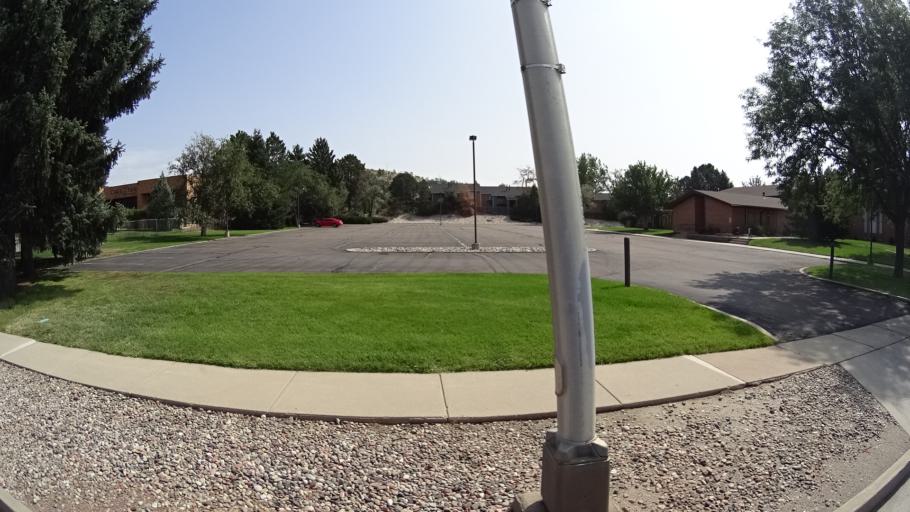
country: US
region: Colorado
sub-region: El Paso County
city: Cimarron Hills
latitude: 38.8584
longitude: -104.7478
